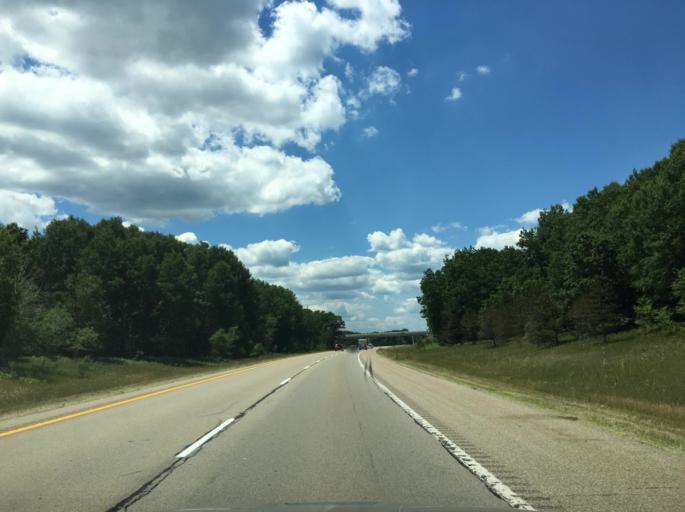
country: US
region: Michigan
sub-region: Clare County
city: Clare
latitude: 43.8749
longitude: -84.8240
